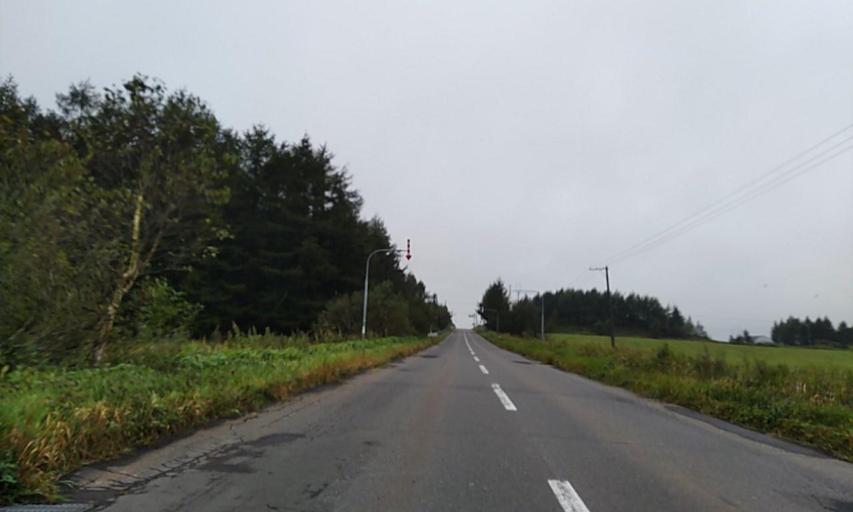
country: JP
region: Hokkaido
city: Shibetsu
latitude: 43.5079
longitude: 144.6662
